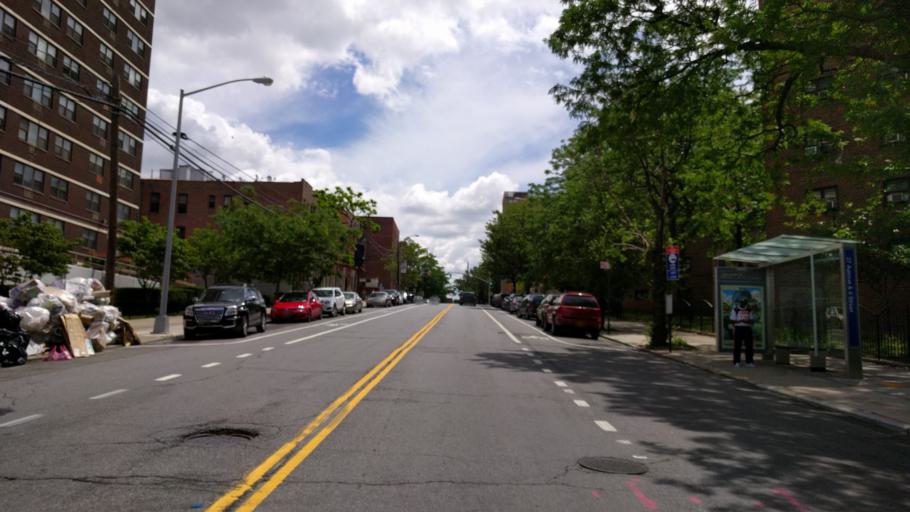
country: US
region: New York
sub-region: Queens County
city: Long Island City
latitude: 40.7746
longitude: -73.9331
